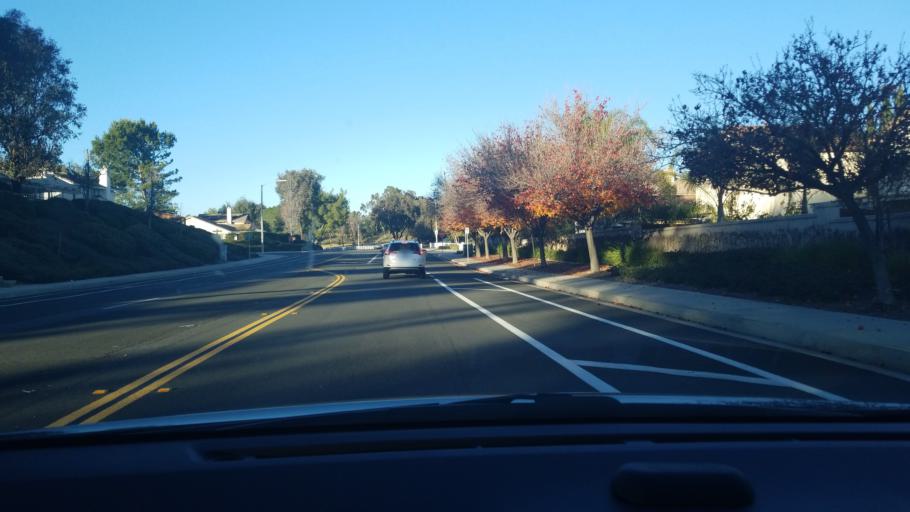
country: US
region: California
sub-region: Riverside County
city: Temecula
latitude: 33.5153
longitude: -117.1223
